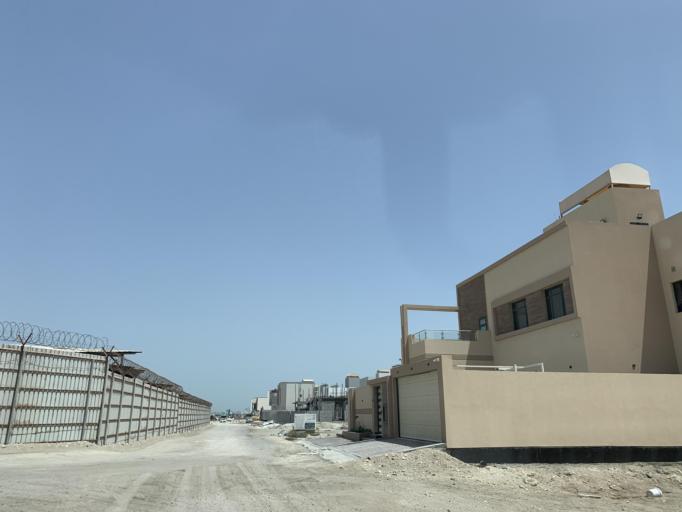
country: BH
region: Northern
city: Sitrah
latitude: 26.1477
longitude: 50.5994
